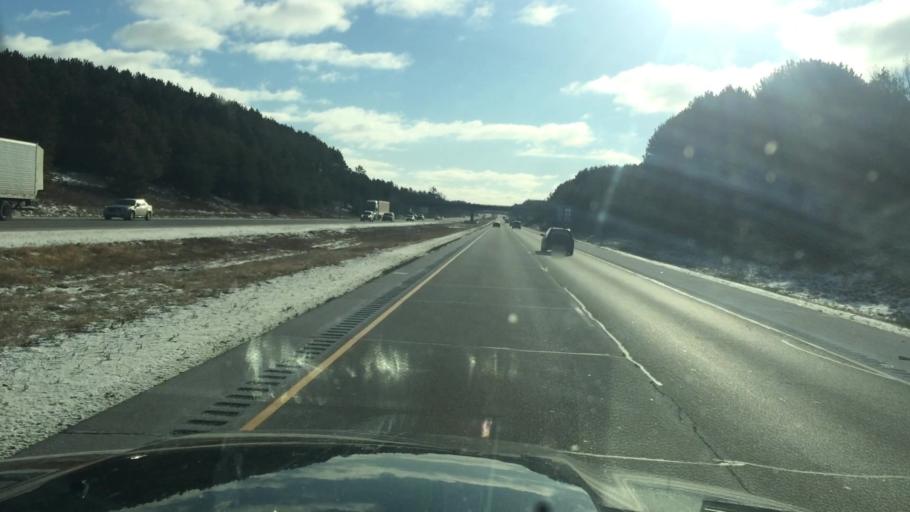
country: US
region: Wisconsin
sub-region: Portage County
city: Stevens Point
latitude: 44.5332
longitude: -89.5371
